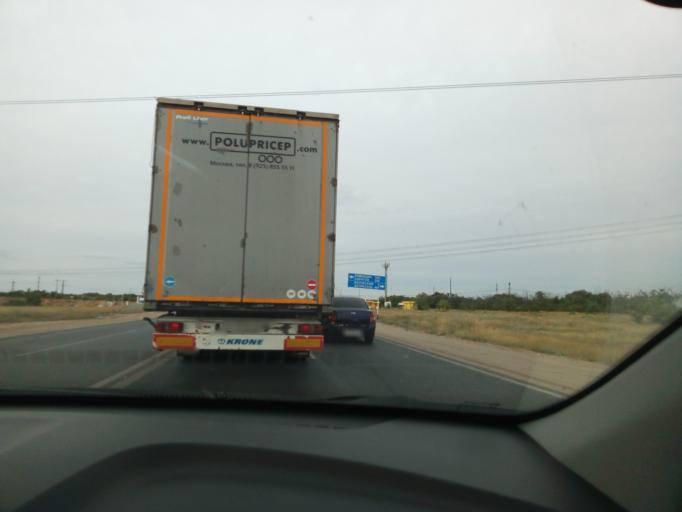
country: RU
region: Volgograd
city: Vodstroy
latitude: 48.8875
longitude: 44.6132
